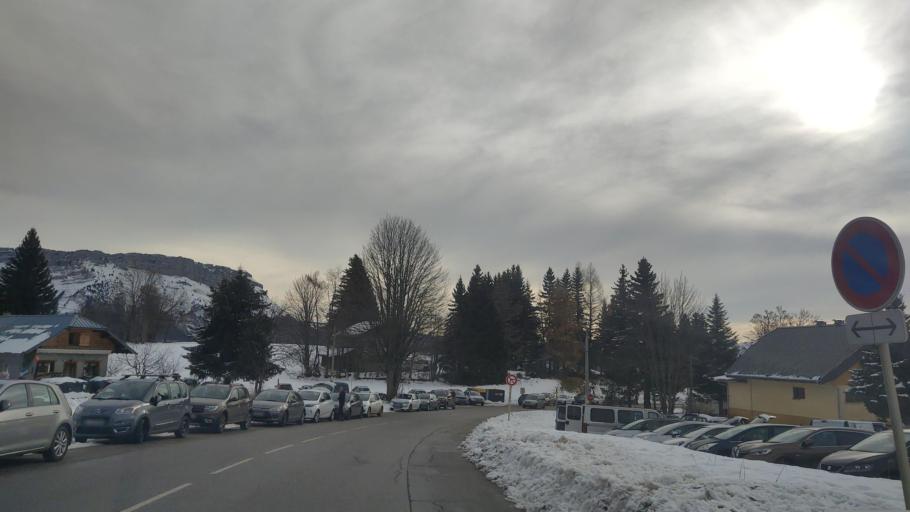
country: FR
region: Rhone-Alpes
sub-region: Departement de la Savoie
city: Mery
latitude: 45.6470
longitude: 5.9857
